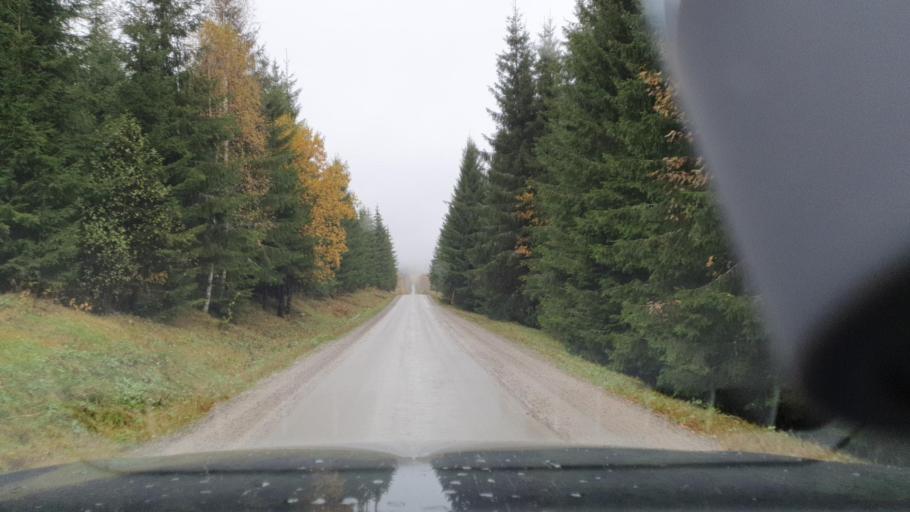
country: SE
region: Vaermland
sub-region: Arvika Kommun
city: Arvika
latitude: 59.7972
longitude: 12.7505
